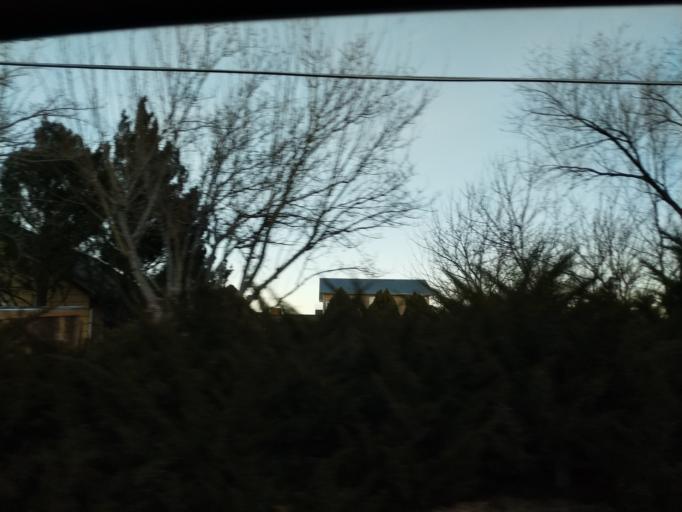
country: US
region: Colorado
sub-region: Mesa County
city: Grand Junction
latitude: 39.1069
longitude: -108.5616
